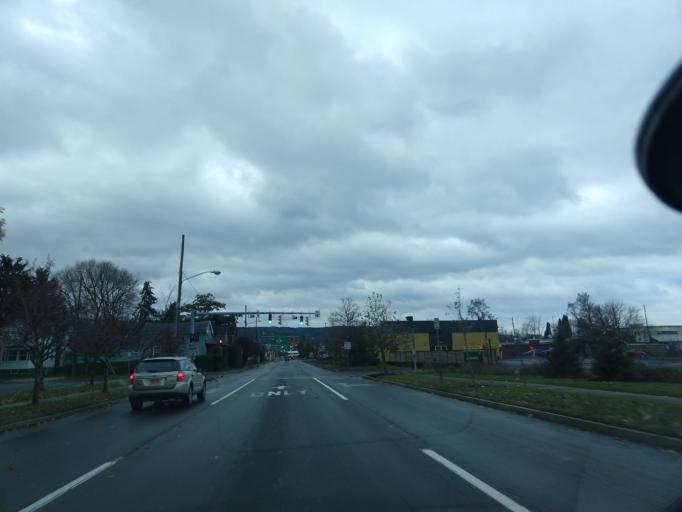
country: US
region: New York
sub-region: Tompkins County
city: Ithaca
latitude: 42.4428
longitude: -76.5107
